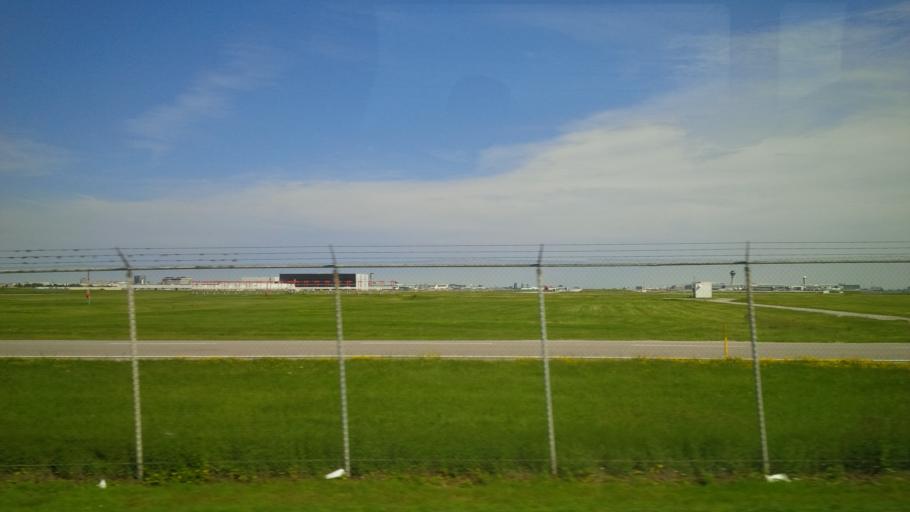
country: CA
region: Ontario
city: Etobicoke
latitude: 43.6970
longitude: -79.6497
